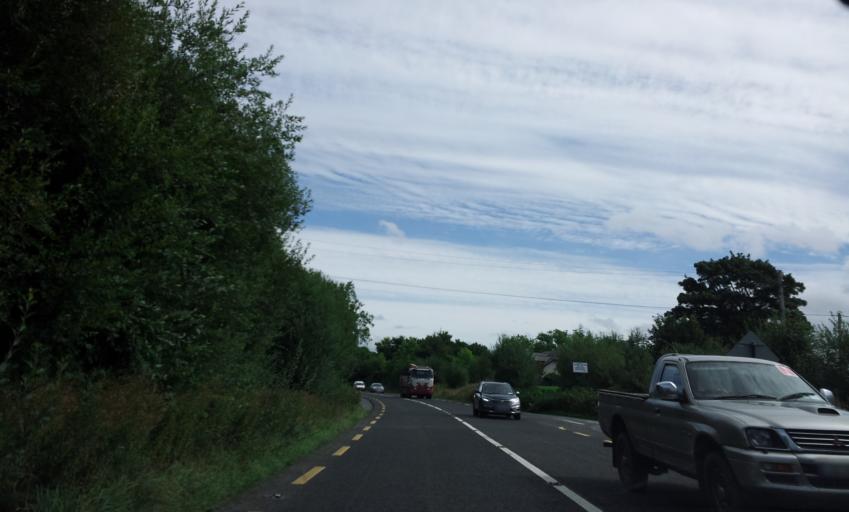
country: IE
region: Munster
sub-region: Ciarrai
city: Cill Airne
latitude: 52.0755
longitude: -9.6491
